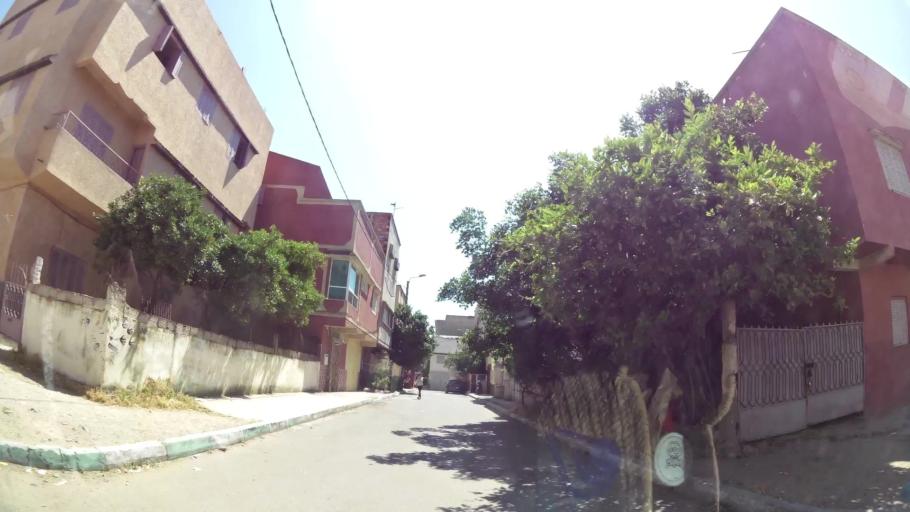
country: MA
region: Gharb-Chrarda-Beni Hssen
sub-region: Kenitra Province
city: Kenitra
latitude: 34.2431
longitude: -6.5547
